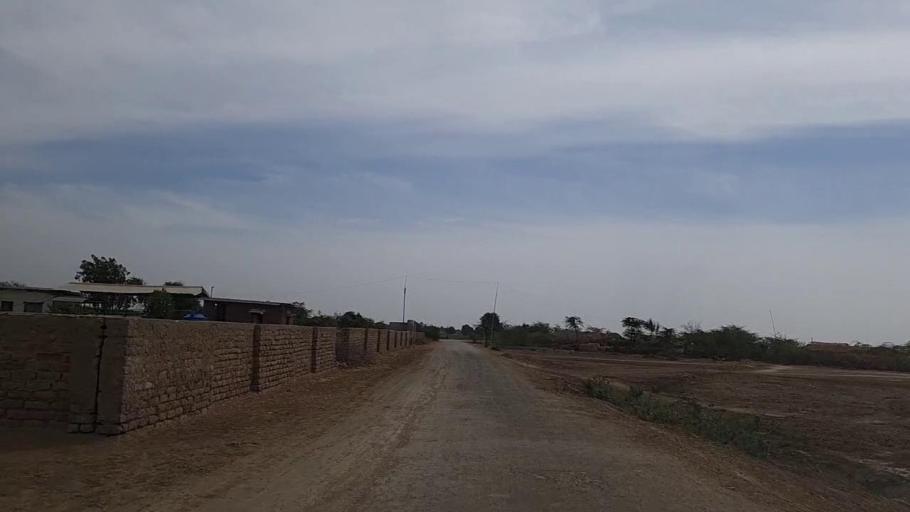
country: PK
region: Sindh
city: Samaro
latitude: 25.3054
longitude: 69.4514
